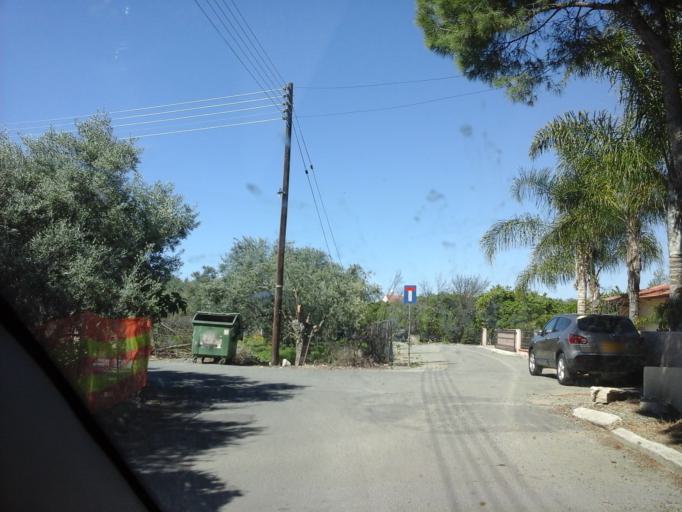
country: CY
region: Larnaka
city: Kolossi
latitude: 34.6699
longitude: 32.9314
